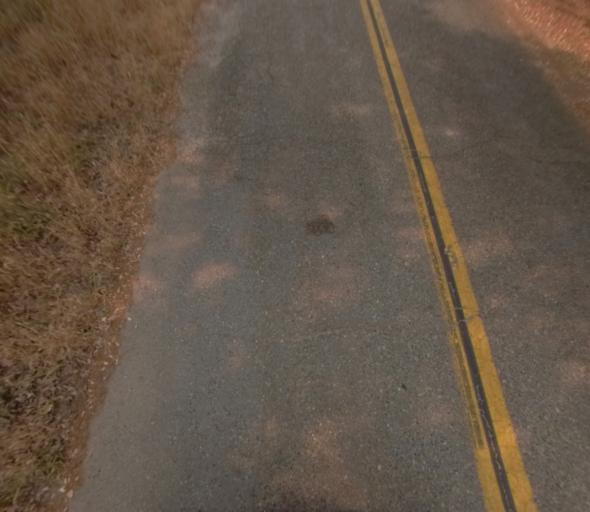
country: US
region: California
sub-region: Madera County
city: Oakhurst
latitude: 37.3012
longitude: -119.5992
